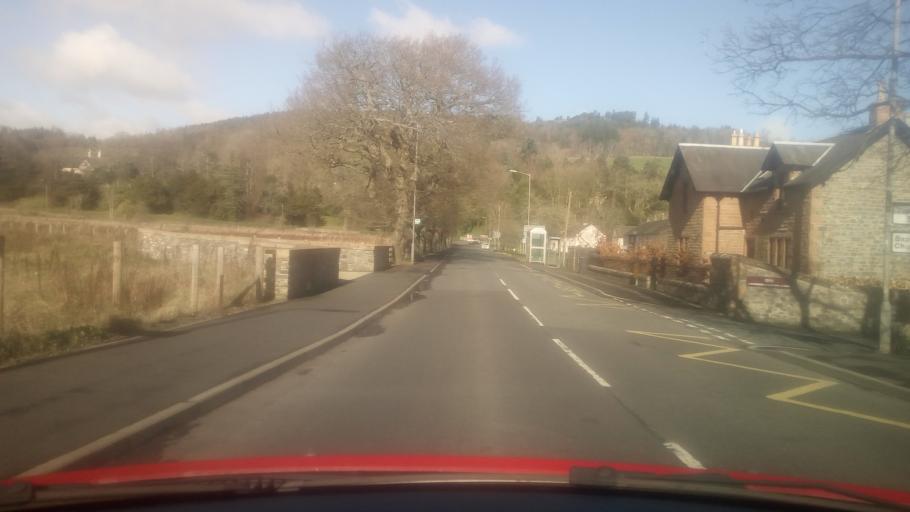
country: GB
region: Scotland
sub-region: The Scottish Borders
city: Selkirk
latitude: 55.5488
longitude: -2.8570
